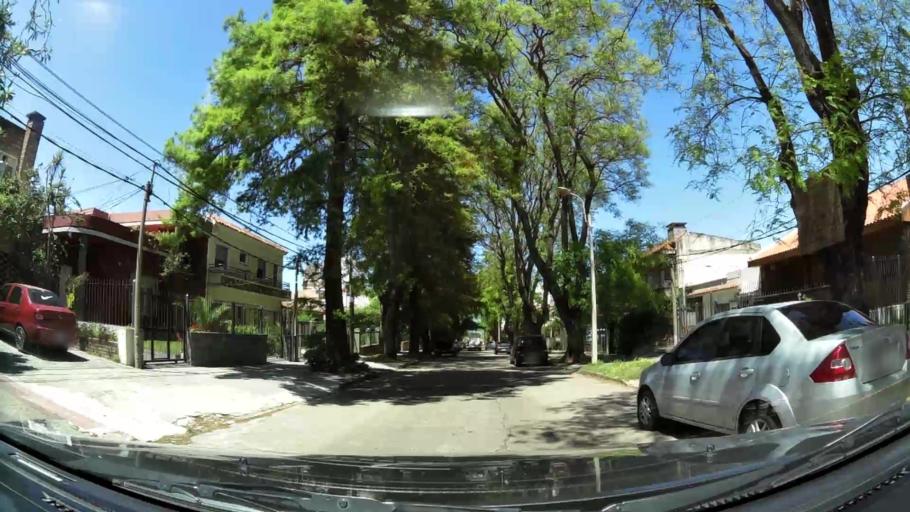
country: UY
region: Canelones
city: Paso de Carrasco
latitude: -34.8932
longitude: -56.1095
